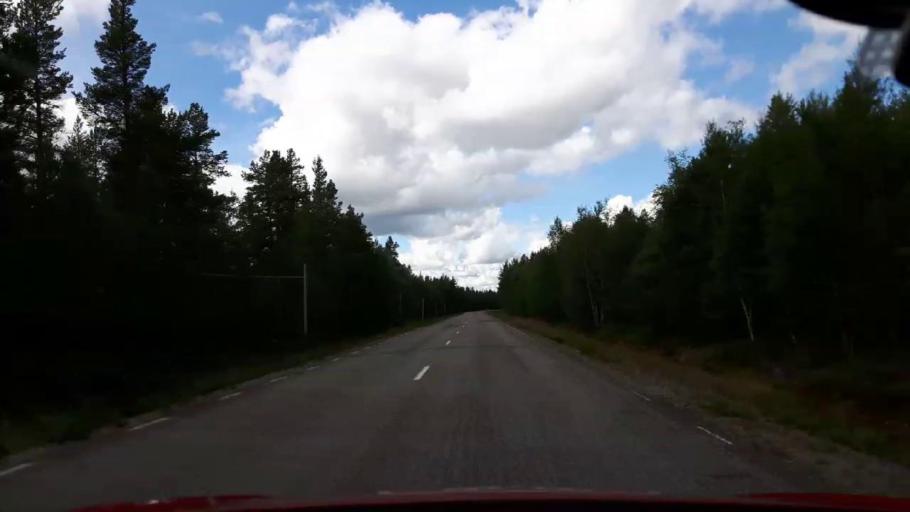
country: SE
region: Jaemtland
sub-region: Harjedalens Kommun
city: Sveg
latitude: 61.8390
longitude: 13.9993
